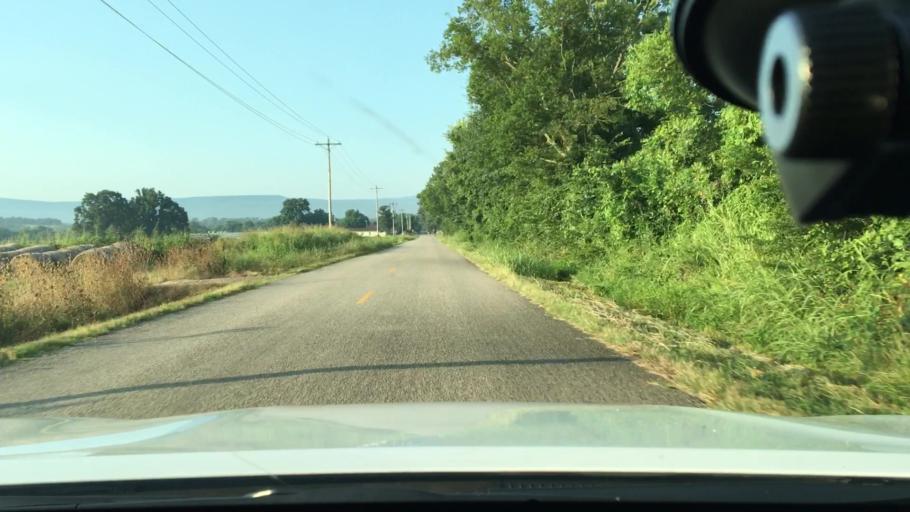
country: US
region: Arkansas
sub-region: Johnson County
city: Coal Hill
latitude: 35.3411
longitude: -93.6137
